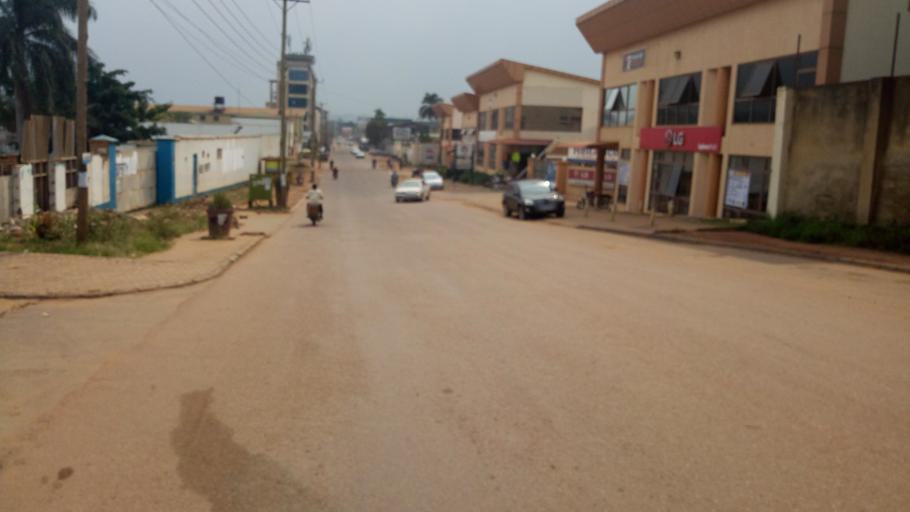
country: UG
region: Central Region
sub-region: Kampala District
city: Kampala
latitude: 0.3138
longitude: 32.6166
